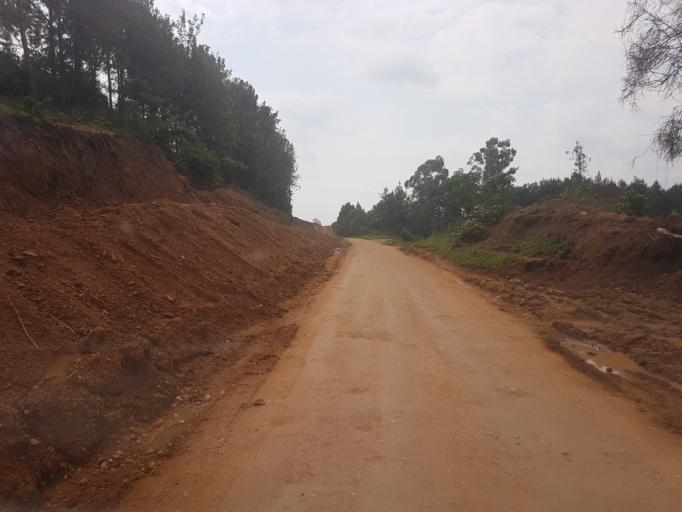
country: UG
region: Western Region
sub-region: Kanungu District
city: Ntungamo
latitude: -0.8250
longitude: 29.7094
